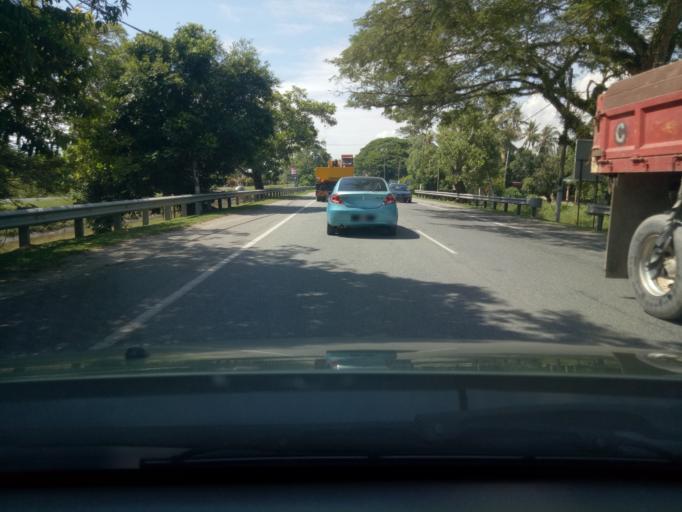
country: MY
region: Kedah
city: Alor Setar
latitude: 5.9661
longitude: 100.4030
